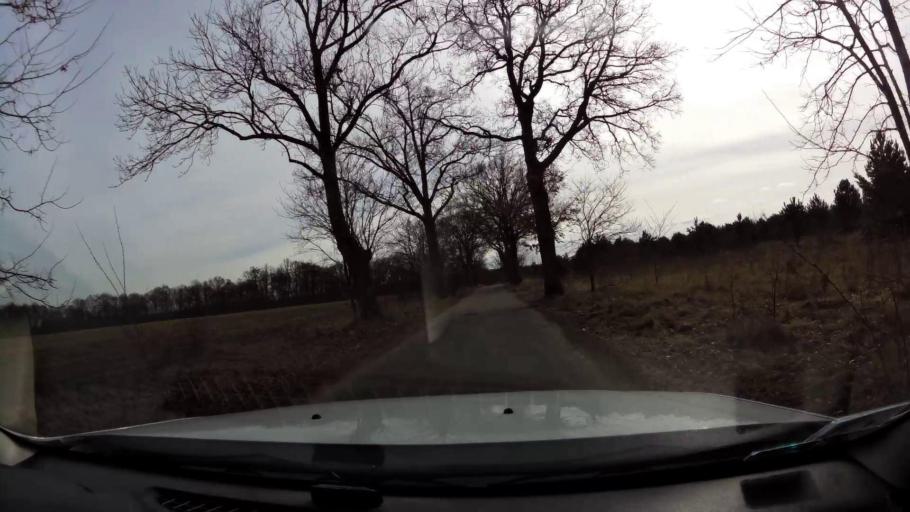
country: PL
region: West Pomeranian Voivodeship
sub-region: Powiat stargardzki
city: Insko
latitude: 53.4478
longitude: 15.6413
